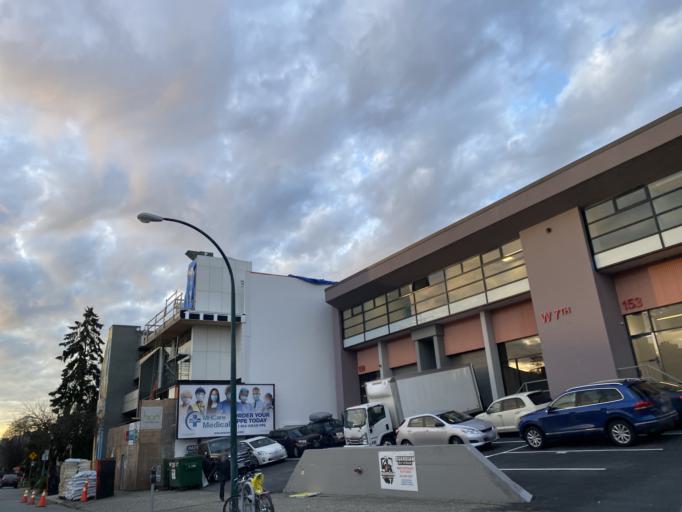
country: CA
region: British Columbia
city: Vancouver
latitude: 49.2648
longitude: -123.1079
